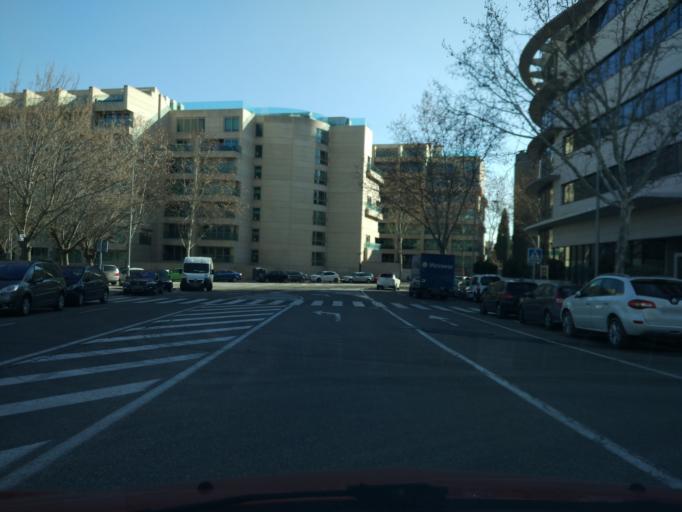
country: ES
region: Madrid
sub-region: Provincia de Madrid
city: San Blas
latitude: 40.4414
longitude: -3.6188
